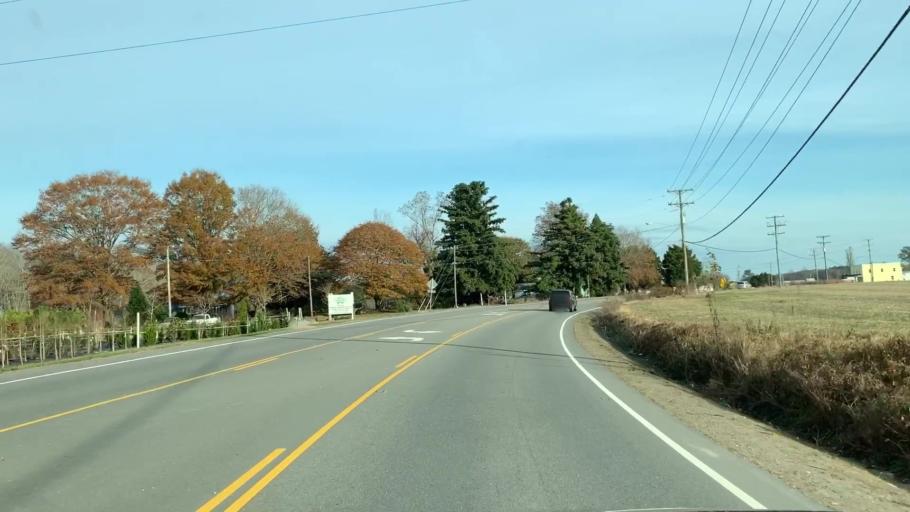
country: US
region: Virginia
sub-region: City of Virginia Beach
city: Virginia Beach
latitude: 36.6917
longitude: -76.0255
